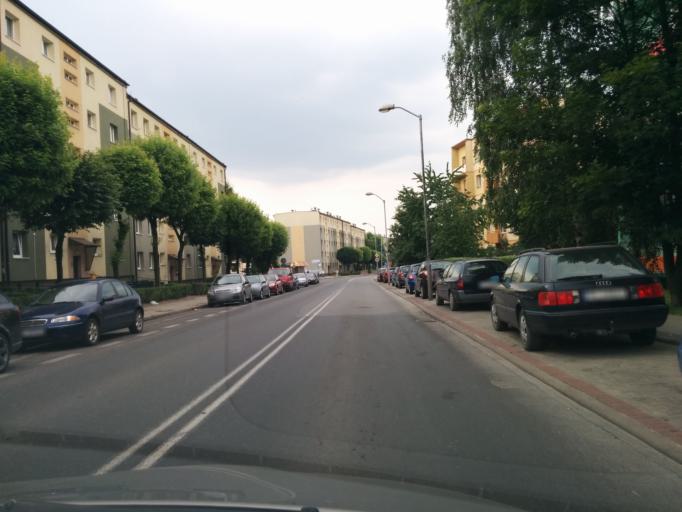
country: PL
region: Silesian Voivodeship
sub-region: Ruda Slaska
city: Ruda Slaska
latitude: 50.2414
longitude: 18.8324
